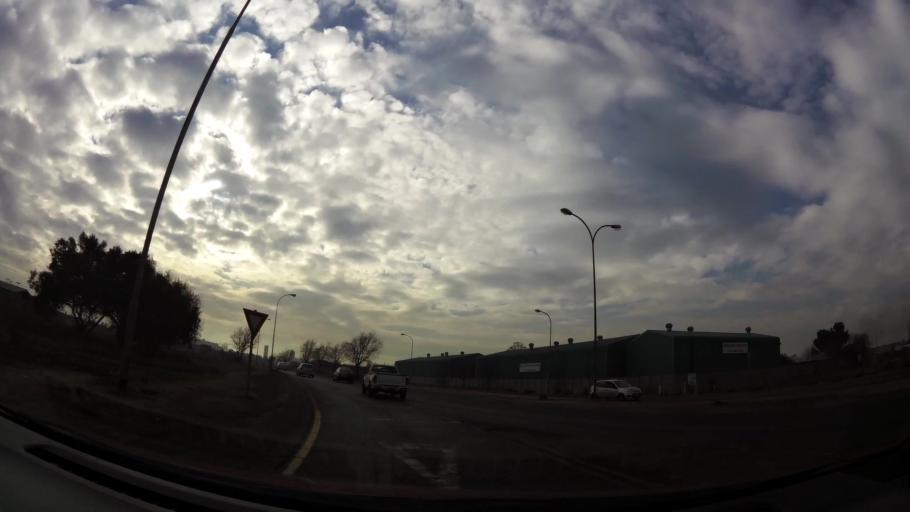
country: ZA
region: Gauteng
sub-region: Sedibeng District Municipality
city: Vanderbijlpark
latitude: -26.6769
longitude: 27.7937
